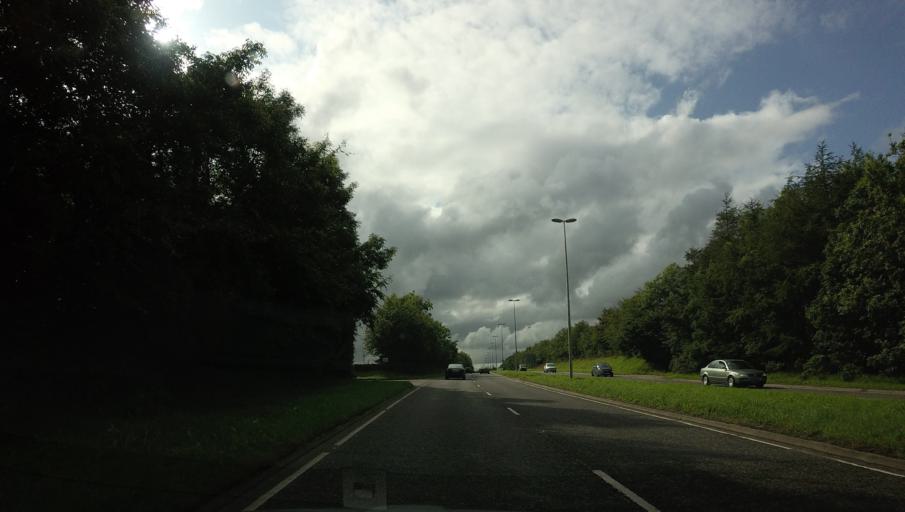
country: GB
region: Scotland
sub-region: Aberdeen City
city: Cults
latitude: 57.1456
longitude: -2.2082
